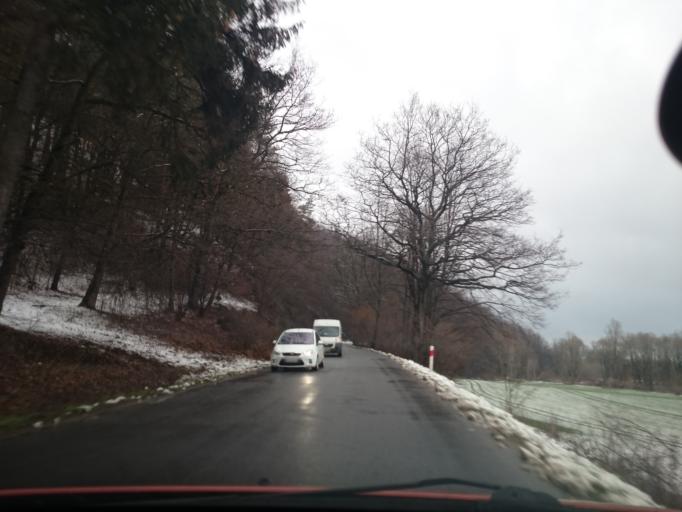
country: PL
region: Lower Silesian Voivodeship
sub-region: Powiat klodzki
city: Klodzko
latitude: 50.4019
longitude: 16.6302
